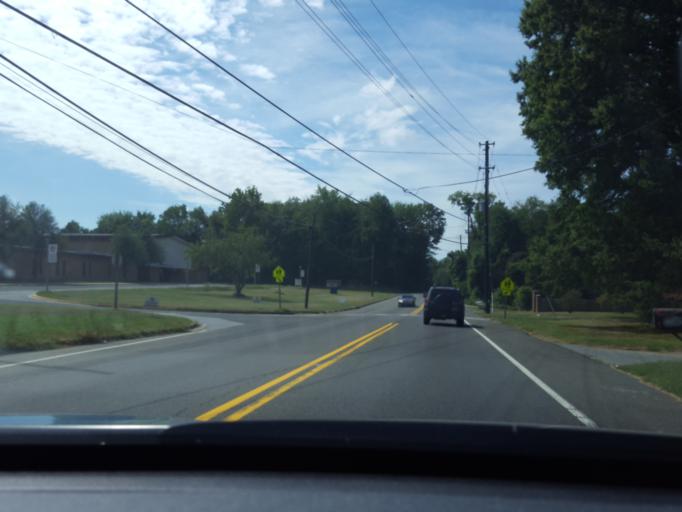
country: US
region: Maryland
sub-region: Prince George's County
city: Mellwood
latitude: 38.7898
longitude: -76.8405
